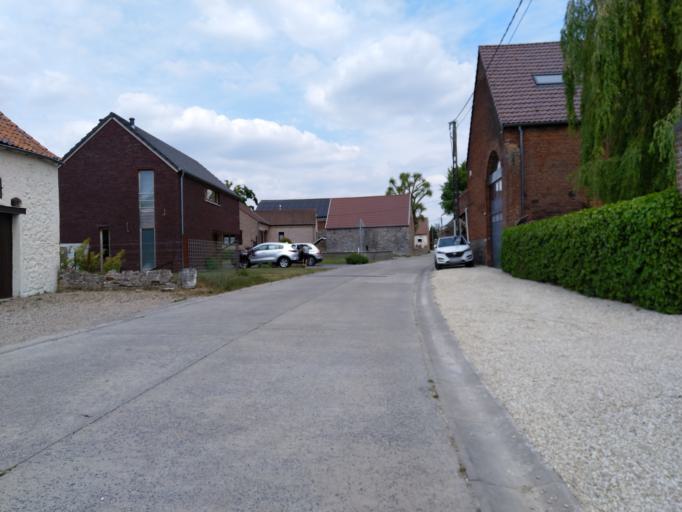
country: BE
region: Wallonia
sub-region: Province du Hainaut
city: Lens
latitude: 50.5840
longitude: 3.9190
